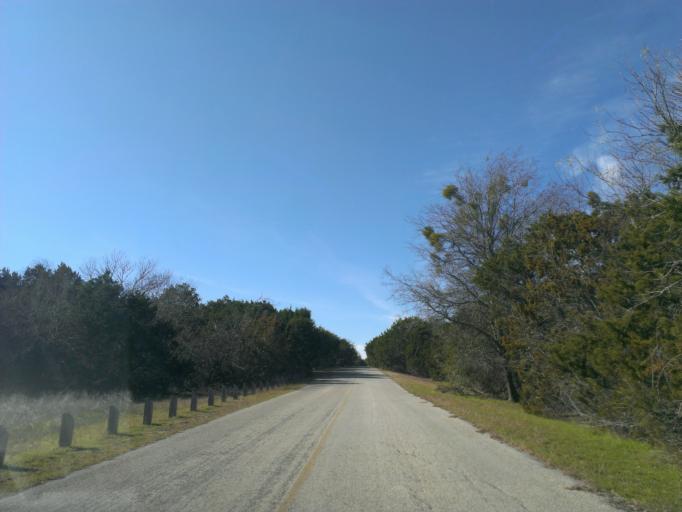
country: US
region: Texas
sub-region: Bell County
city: Salado
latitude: 31.0160
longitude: -97.5306
